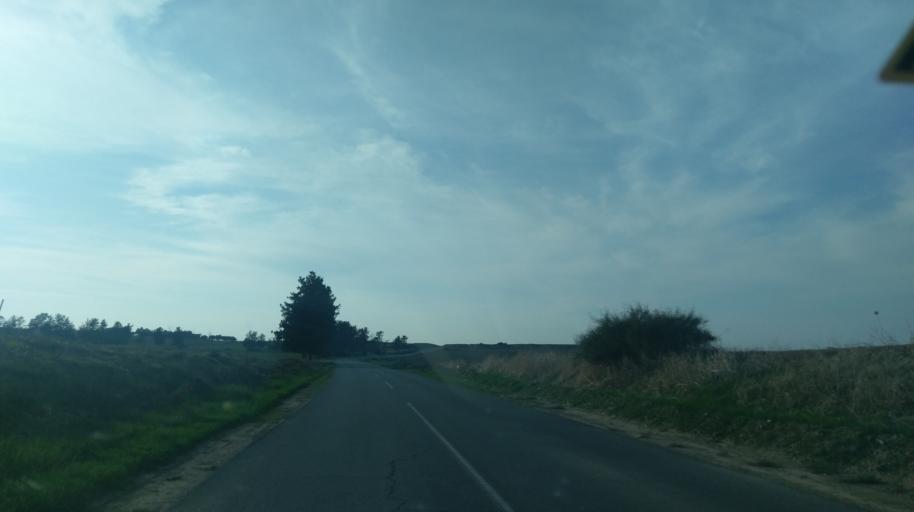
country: CY
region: Ammochostos
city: Achna
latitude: 35.1026
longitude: 33.7786
